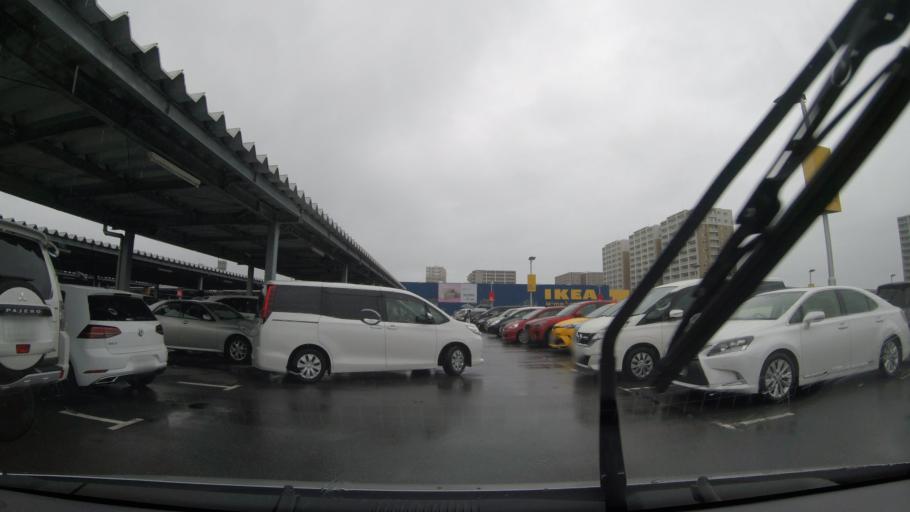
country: JP
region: Fukuoka
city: Shingu
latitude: 33.7091
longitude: 130.4517
